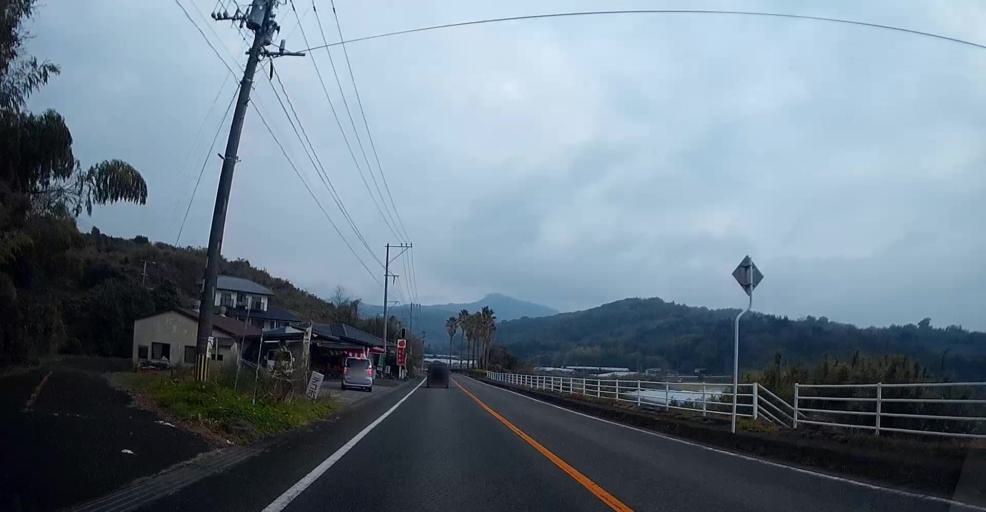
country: JP
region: Kumamoto
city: Matsubase
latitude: 32.6255
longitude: 130.5403
